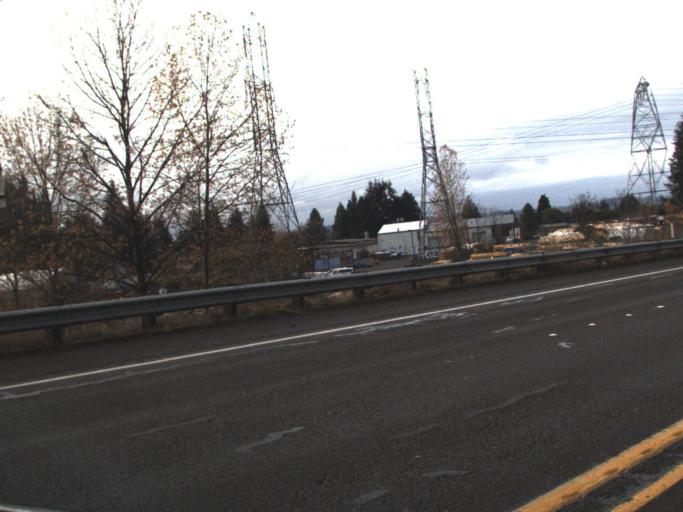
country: US
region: Washington
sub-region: Snohomish County
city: Fobes Hill
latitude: 47.9543
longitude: -122.1139
